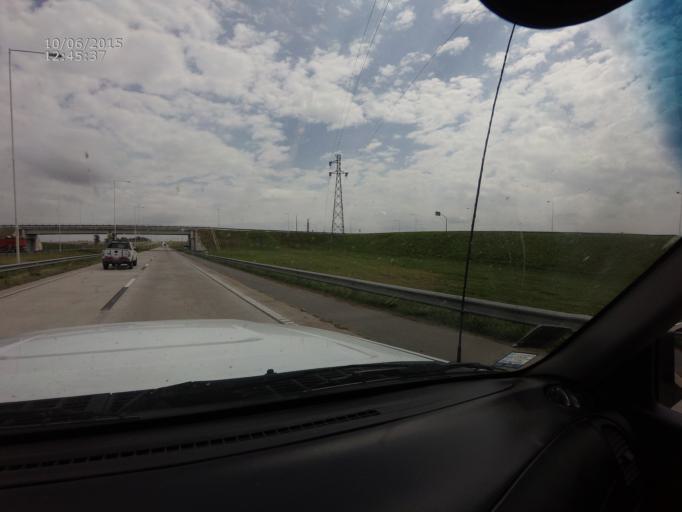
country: AR
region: Santa Fe
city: Canada de Gomez
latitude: -32.8467
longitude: -61.3900
